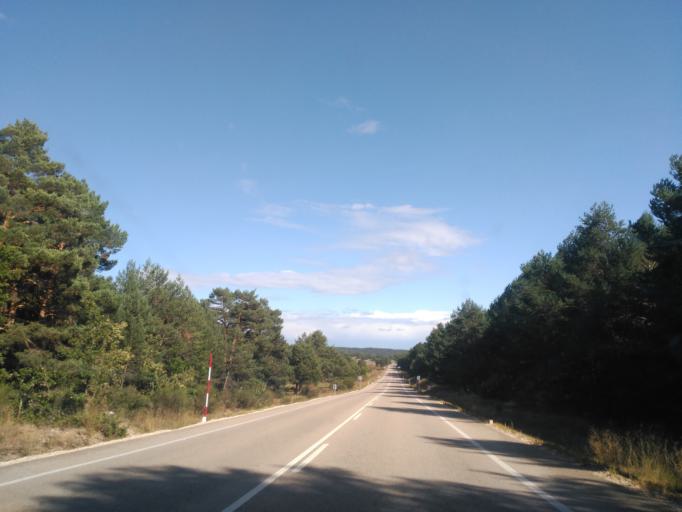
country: ES
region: Castille and Leon
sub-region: Provincia de Burgos
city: Rabanera del Pinar
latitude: 41.8882
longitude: -3.2423
